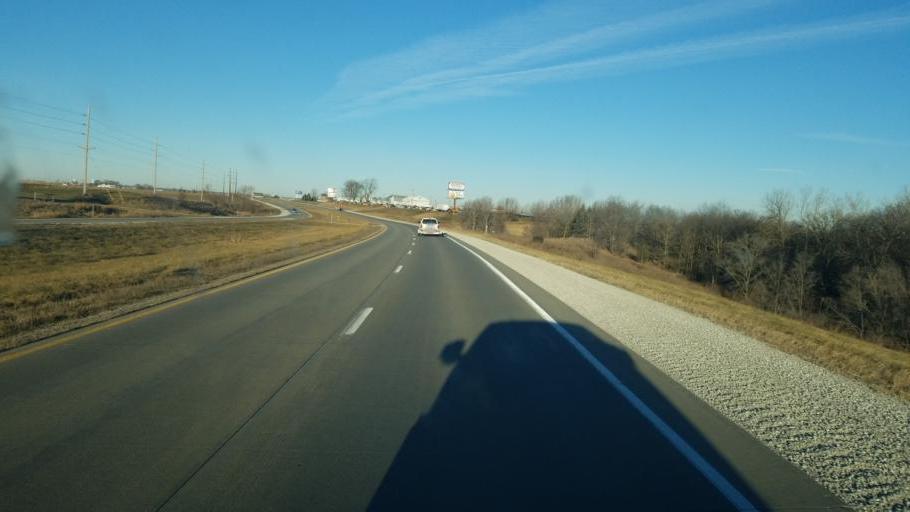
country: US
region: Iowa
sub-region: Marion County
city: Pella
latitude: 41.3864
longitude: -92.8260
